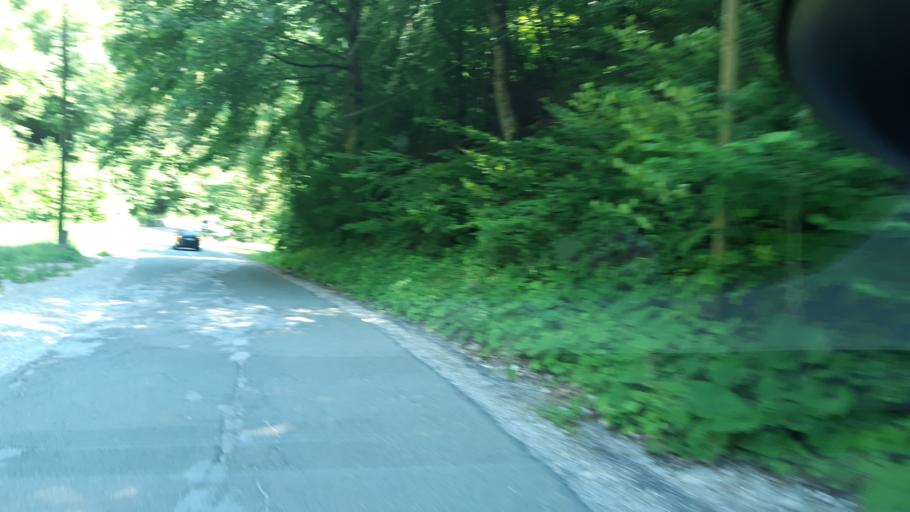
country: SI
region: Cerklje na Gorenjskem
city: Cerklje na Gorenjskem
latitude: 46.2801
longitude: 14.4960
